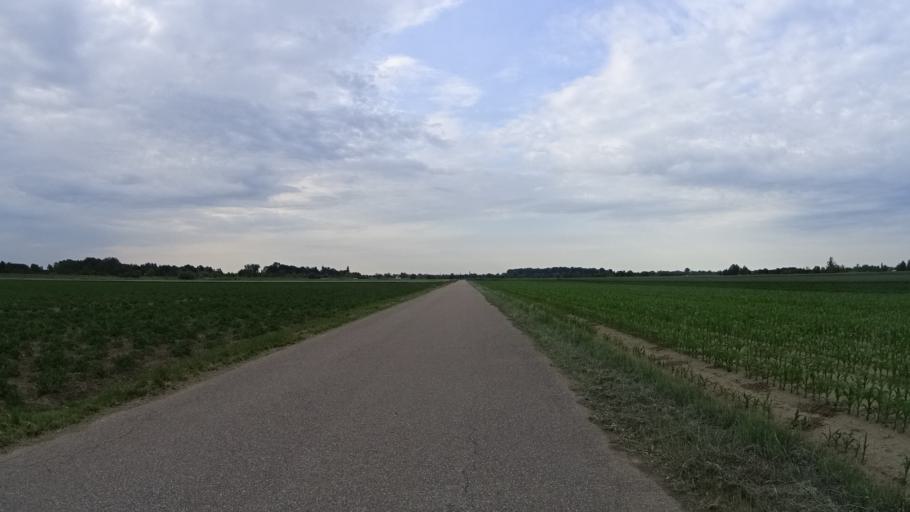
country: DE
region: Bavaria
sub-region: Lower Bavaria
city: Kirchroth
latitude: 48.9406
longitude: 12.5387
